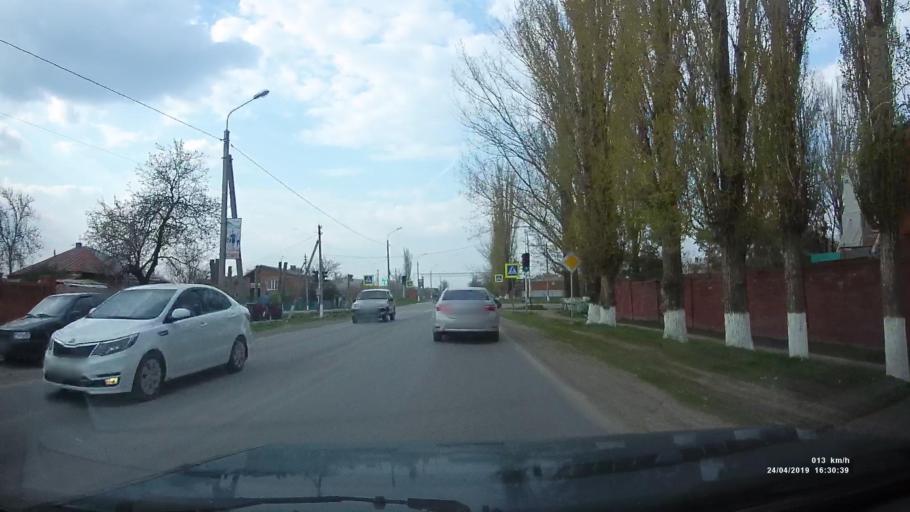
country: RU
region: Rostov
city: Orlovskiy
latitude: 46.8756
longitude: 42.0384
